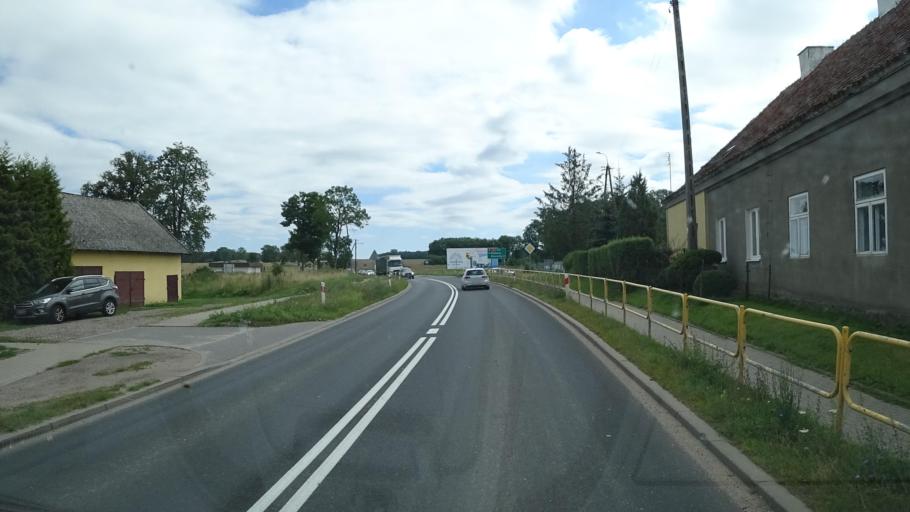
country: PL
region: Warmian-Masurian Voivodeship
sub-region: Powiat elcki
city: Stare Juchy
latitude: 53.7914
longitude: 22.2020
